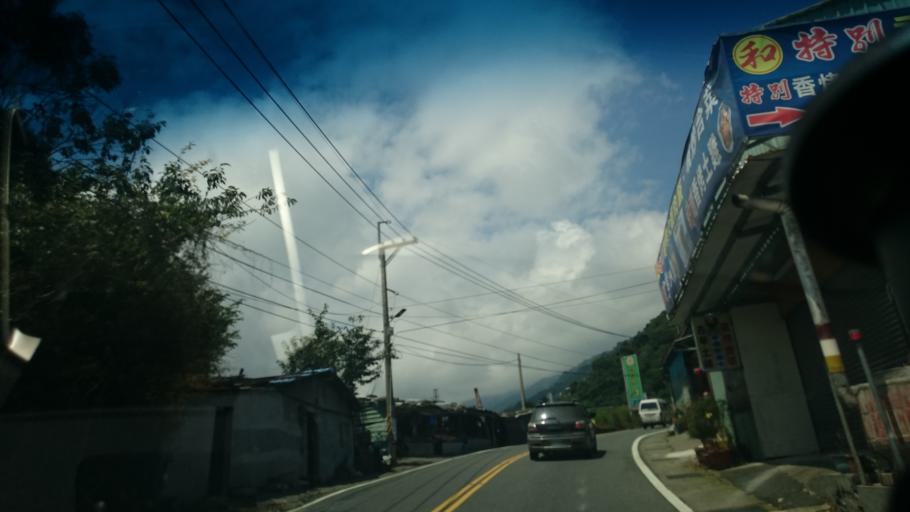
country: TW
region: Taiwan
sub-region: Nantou
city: Puli
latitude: 24.0344
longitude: 121.1420
